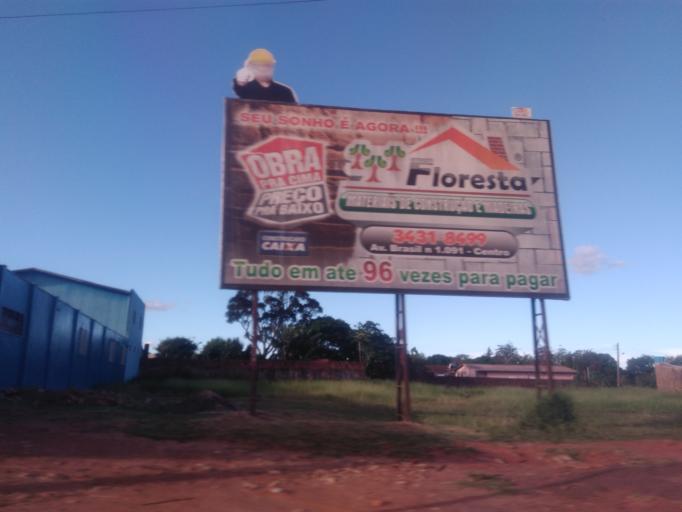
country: BR
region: Mato Grosso do Sul
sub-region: Ponta Pora
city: Ponta Pora
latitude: -22.5054
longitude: -55.7296
